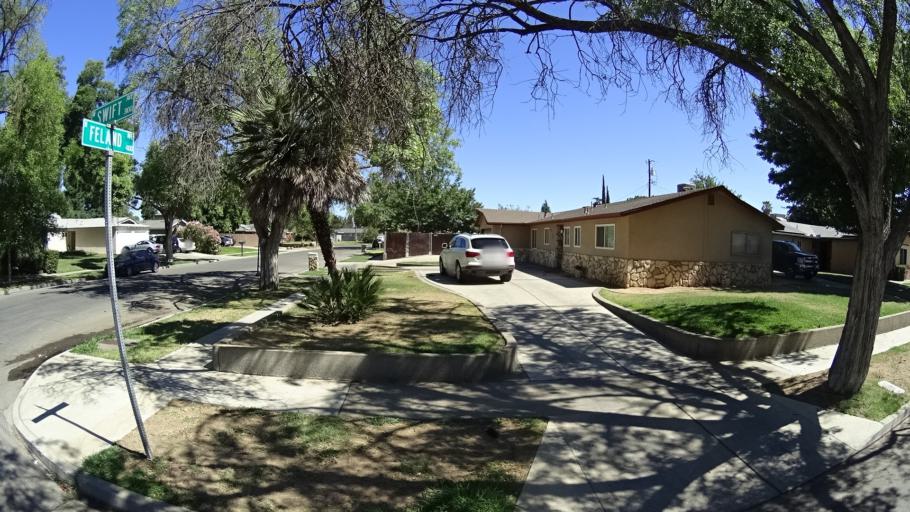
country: US
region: California
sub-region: Fresno County
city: West Park
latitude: 36.7960
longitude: -119.8482
